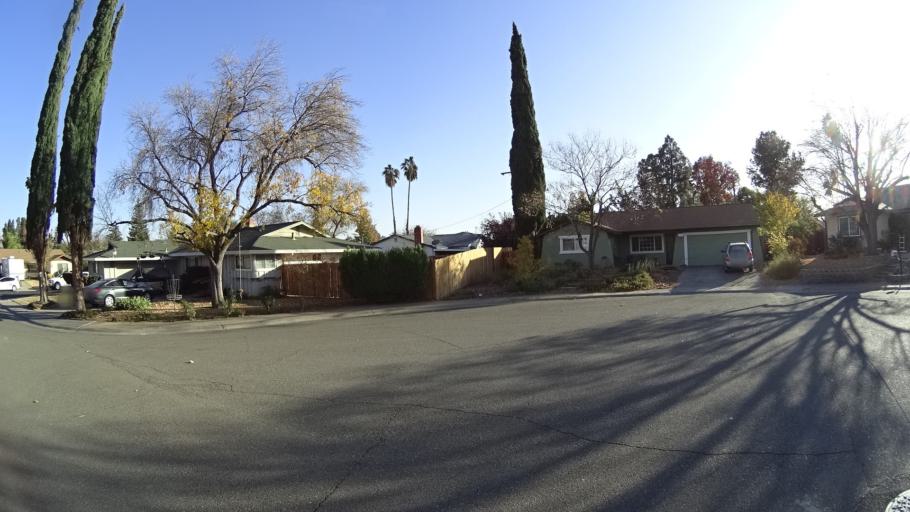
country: US
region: California
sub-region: Sacramento County
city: Citrus Heights
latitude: 38.6991
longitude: -121.2932
